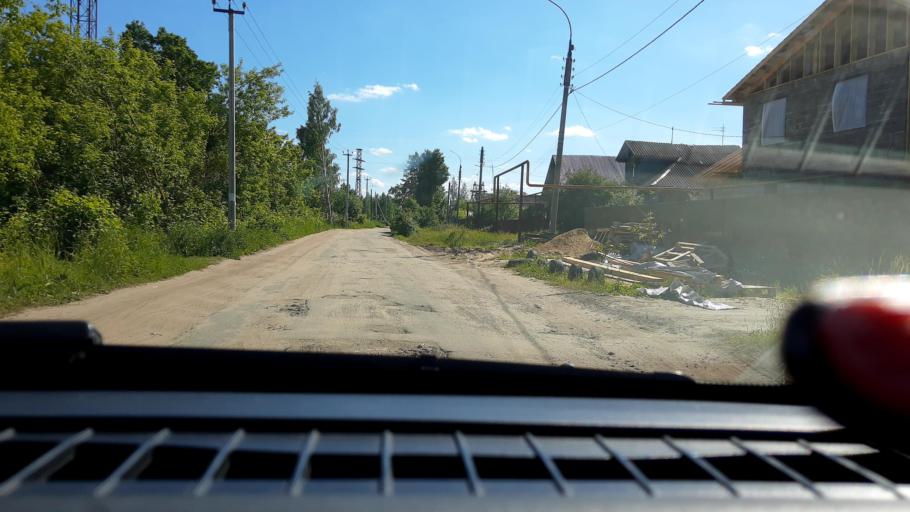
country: RU
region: Nizjnij Novgorod
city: Gidrotorf
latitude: 56.5186
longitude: 43.5400
